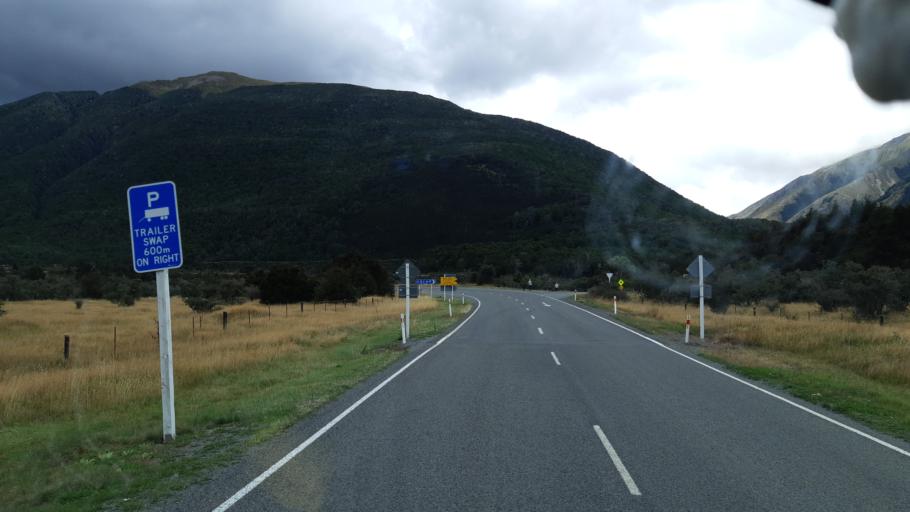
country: NZ
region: Canterbury
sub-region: Hurunui District
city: Amberley
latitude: -42.5165
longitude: 172.3824
